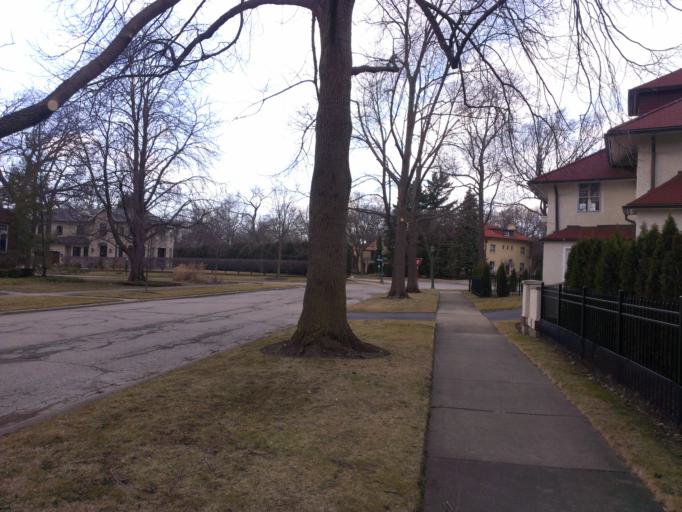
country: US
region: Illinois
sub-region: Cook County
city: Kenilworth
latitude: 42.0794
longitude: -87.6936
